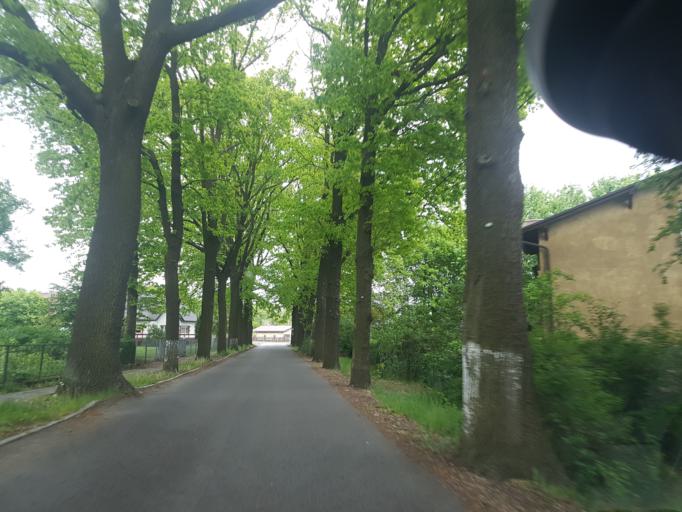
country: DE
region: Brandenburg
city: Neupetershain
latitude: 51.6077
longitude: 14.1608
